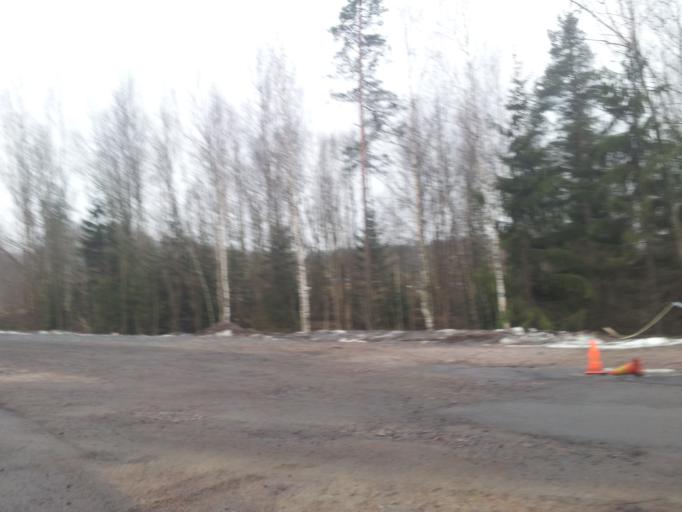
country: FI
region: Uusimaa
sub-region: Helsinki
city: Koukkuniemi
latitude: 60.1552
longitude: 24.7130
